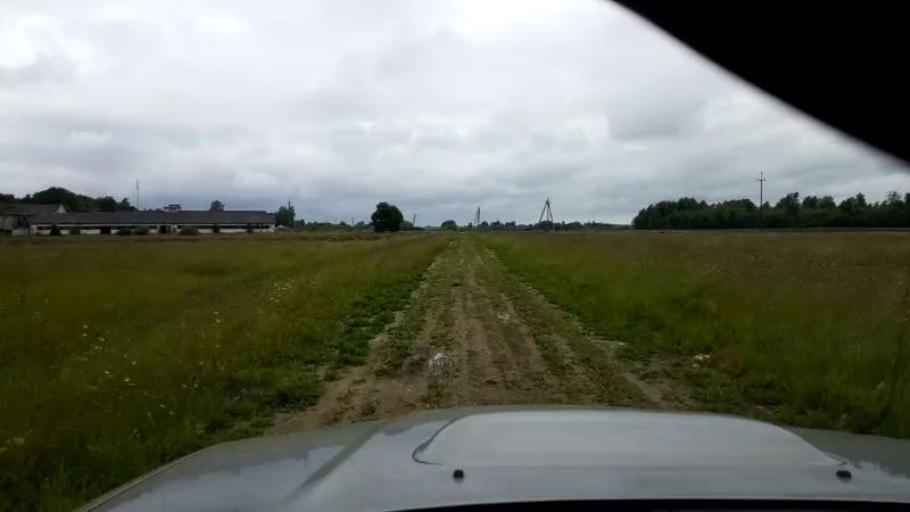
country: EE
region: Paernumaa
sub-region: Halinga vald
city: Parnu-Jaagupi
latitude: 58.5319
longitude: 24.5950
